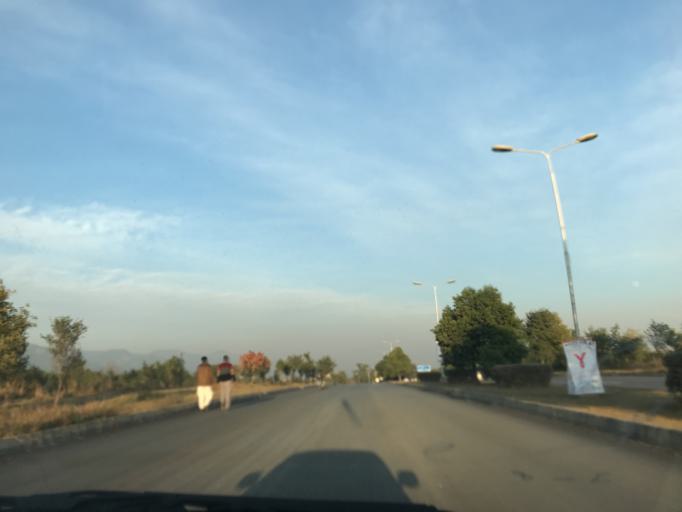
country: PK
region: Islamabad
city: Islamabad
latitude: 33.6981
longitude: 72.9979
